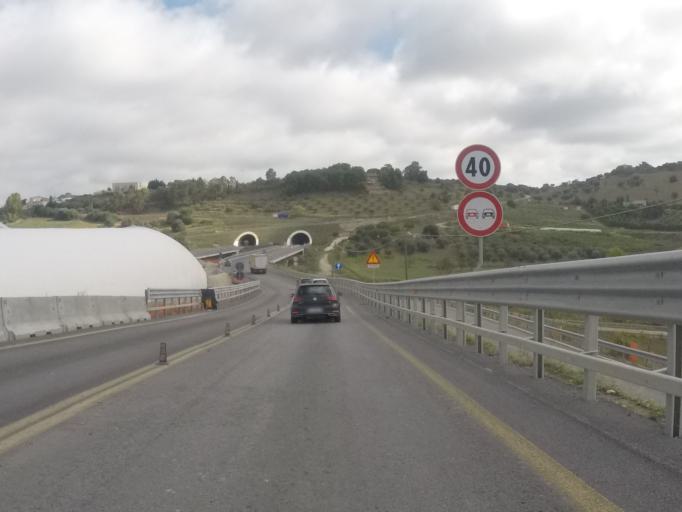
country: IT
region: Sicily
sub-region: Provincia di Caltanissetta
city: San Cataldo
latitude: 37.4570
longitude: 13.9930
